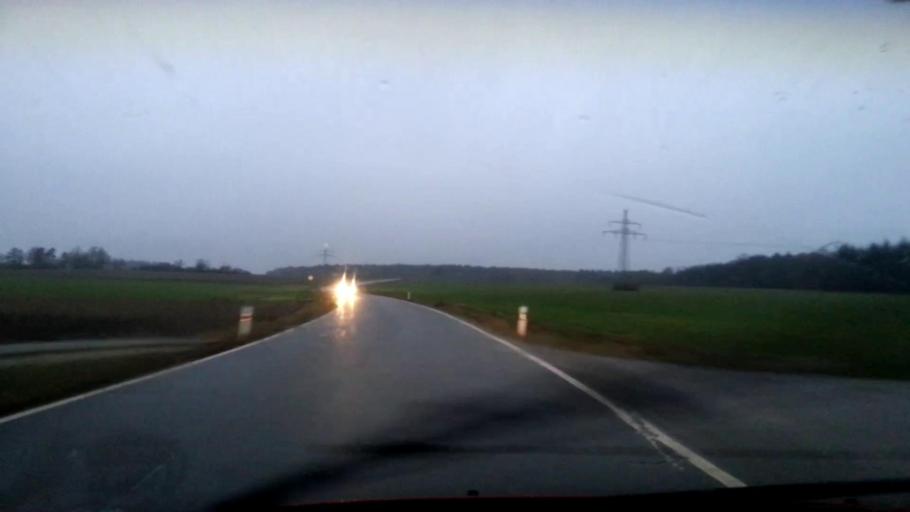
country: DE
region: Bavaria
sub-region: Upper Franconia
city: Konigsfeld
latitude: 49.9545
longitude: 11.1475
